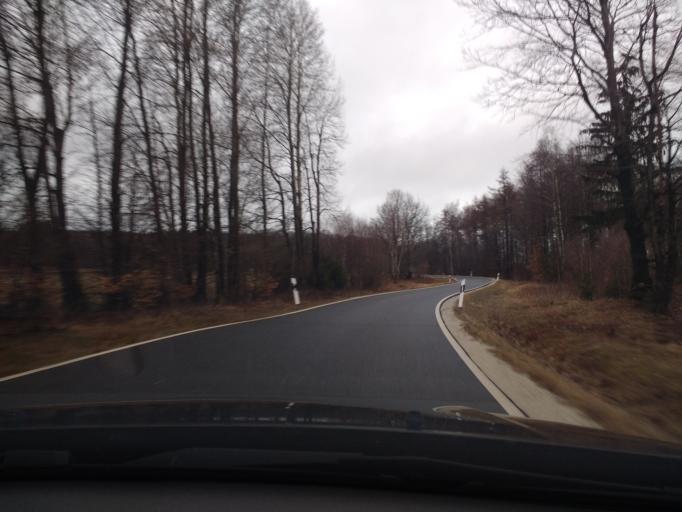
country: DE
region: Rheinland-Pfalz
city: Borfink
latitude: 49.6709
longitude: 7.0419
